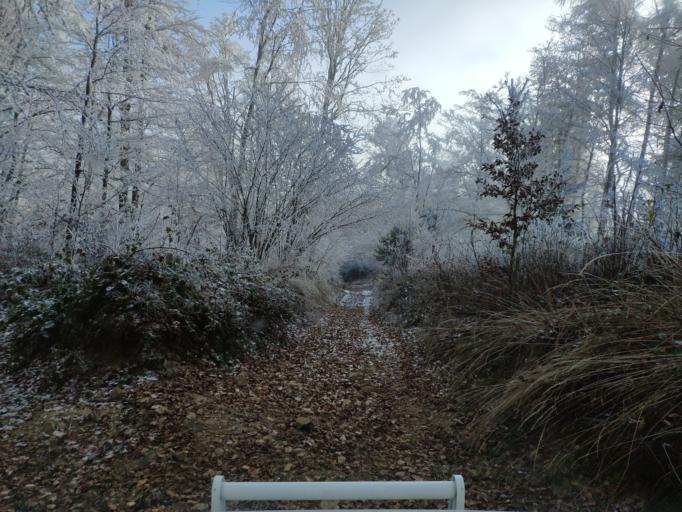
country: SK
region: Kosicky
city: Dobsina
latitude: 48.8137
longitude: 20.4788
